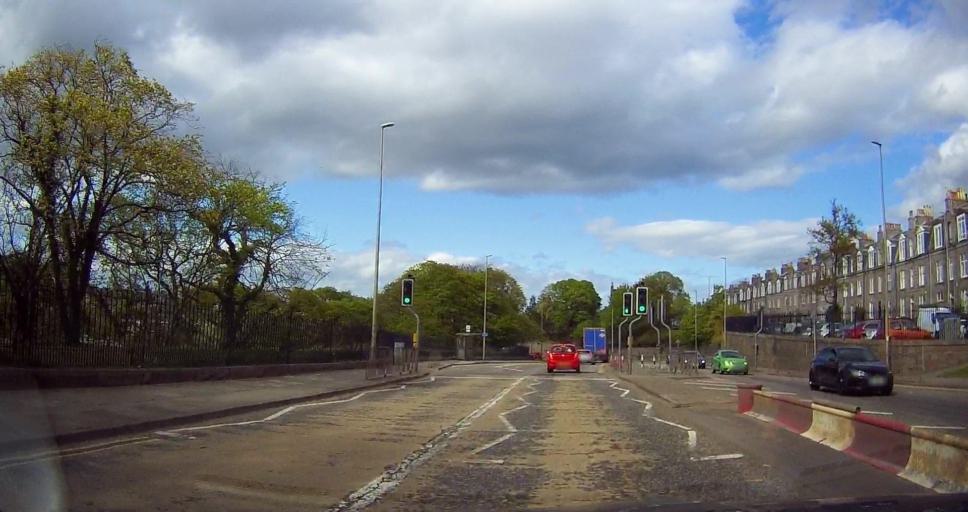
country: GB
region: Scotland
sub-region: Aberdeen City
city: Aberdeen
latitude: 57.1339
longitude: -2.0944
